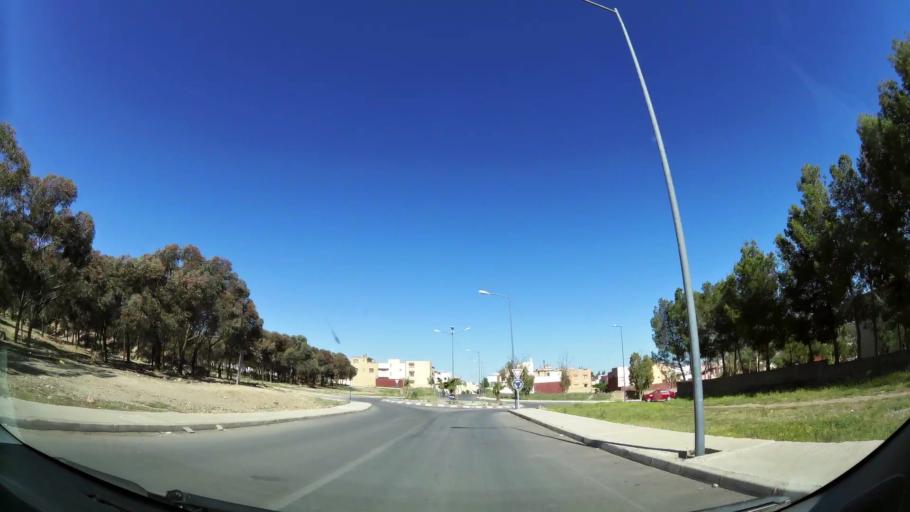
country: MA
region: Oriental
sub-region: Oujda-Angad
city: Oujda
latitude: 34.6482
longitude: -1.9018
